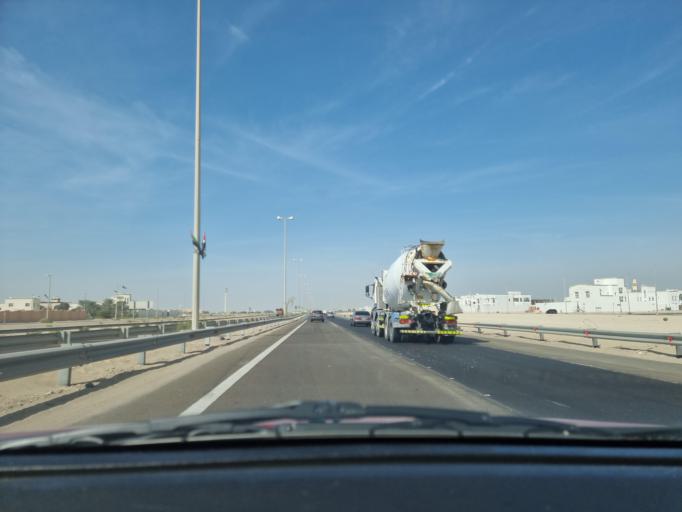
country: AE
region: Abu Dhabi
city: Abu Dhabi
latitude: 24.3608
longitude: 54.6664
